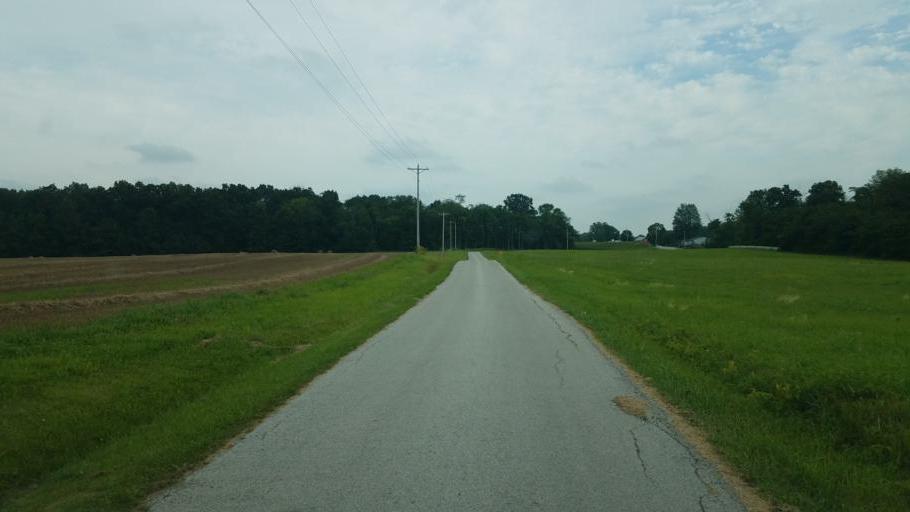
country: US
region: Ohio
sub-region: Morrow County
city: Cardington
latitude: 40.4922
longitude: -82.9512
